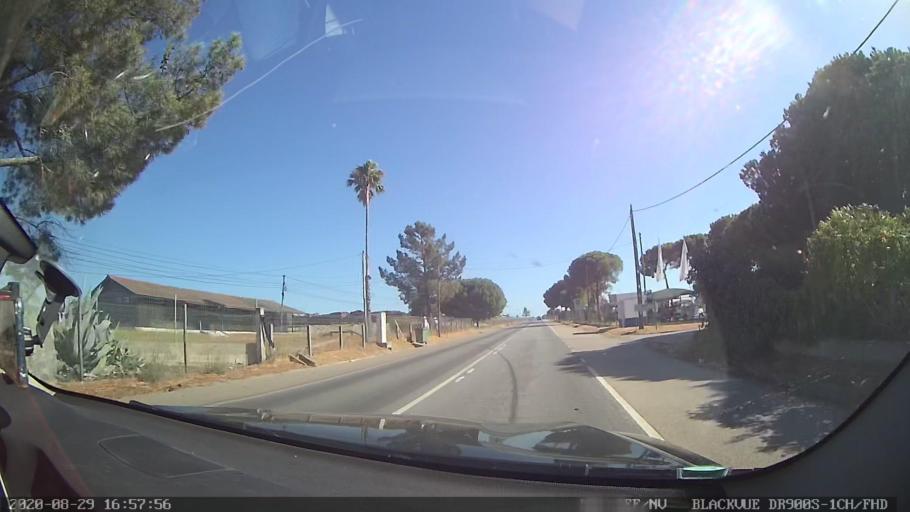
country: PT
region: Setubal
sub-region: Alcacer do Sal
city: Alcacer do Sal
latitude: 38.4004
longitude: -8.5149
